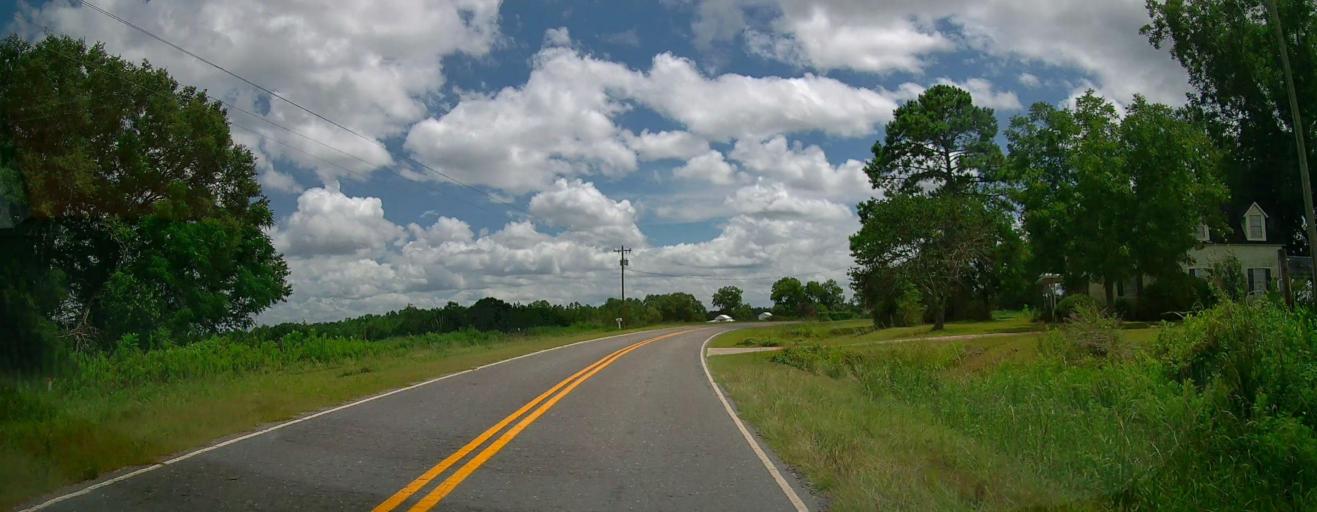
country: US
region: Georgia
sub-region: Ben Hill County
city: Fitzgerald
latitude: 31.6660
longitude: -83.4014
